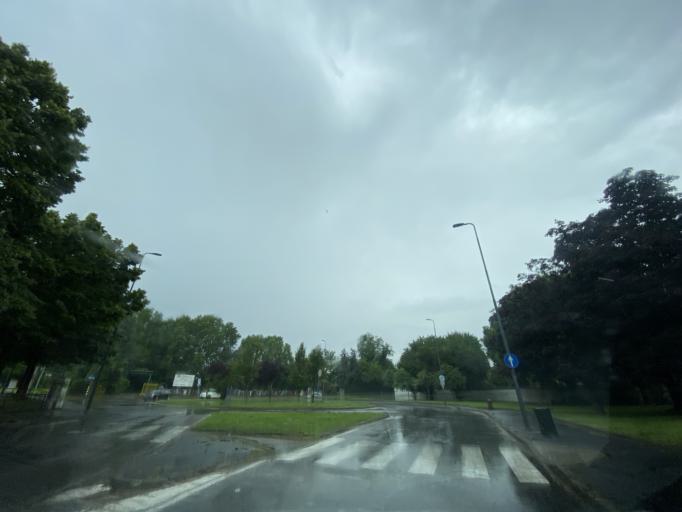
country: IT
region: Lombardy
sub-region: Citta metropolitana di Milano
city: Bresso
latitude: 45.5289
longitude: 9.1794
